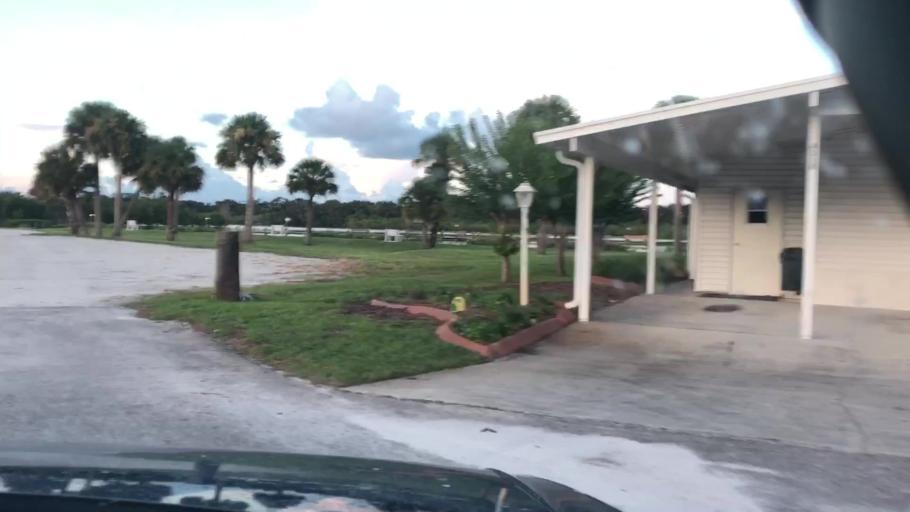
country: US
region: Florida
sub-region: Volusia County
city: Oak Hill
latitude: 28.9159
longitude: -80.8615
